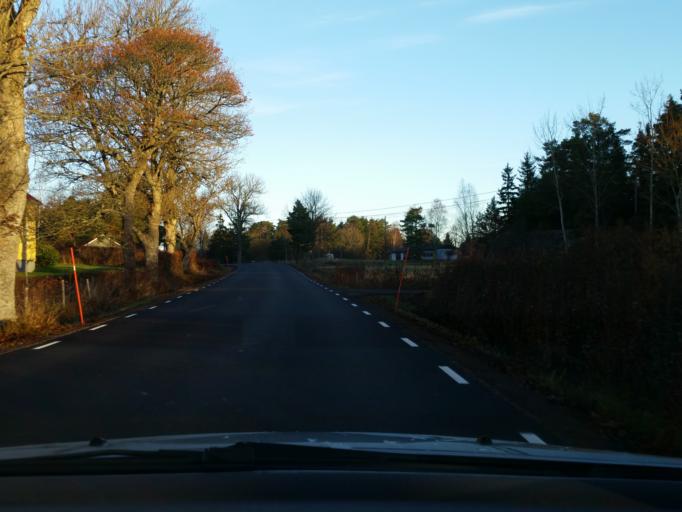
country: AX
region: Alands landsbygd
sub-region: Sund
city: Sund
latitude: 60.2376
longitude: 20.0728
